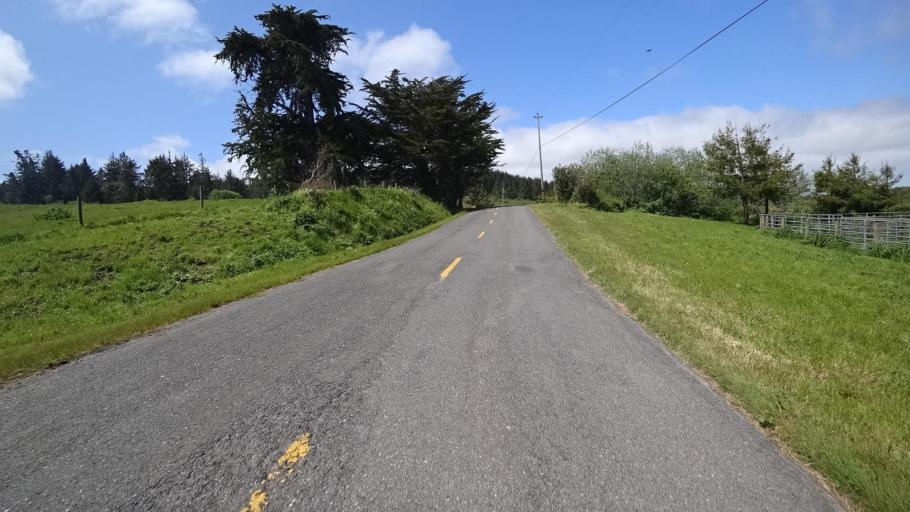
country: US
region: California
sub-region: Humboldt County
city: Humboldt Hill
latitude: 40.6689
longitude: -124.2065
